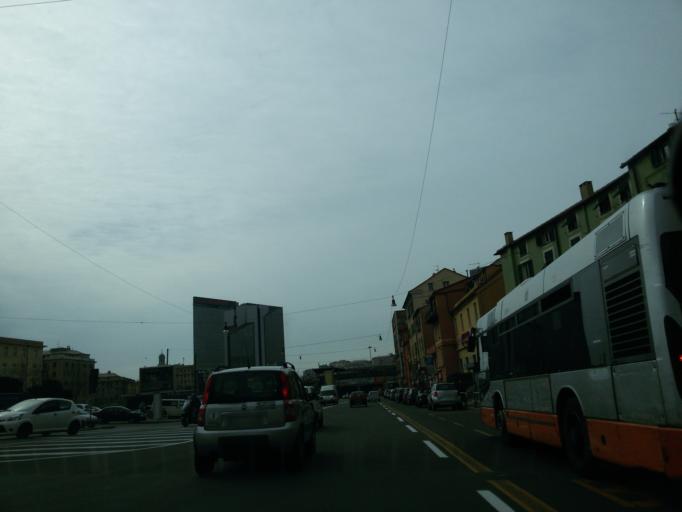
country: IT
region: Liguria
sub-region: Provincia di Genova
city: Genoa
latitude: 44.4088
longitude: 8.9506
